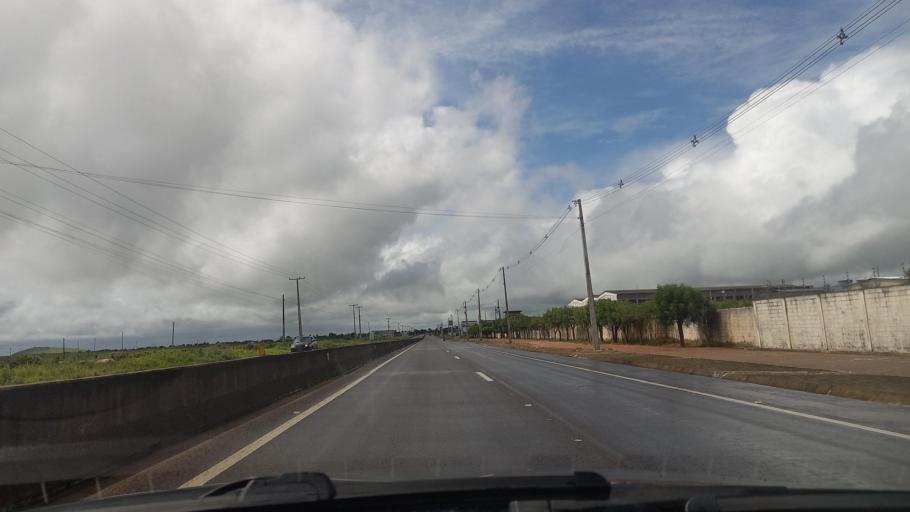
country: BR
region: Alagoas
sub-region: Limoeiro De Anadia
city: Limoeiro de Anadia
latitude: -9.7606
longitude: -36.5448
